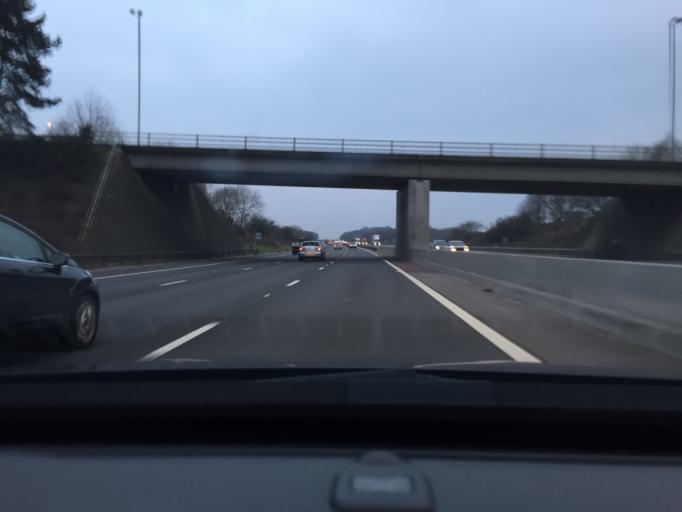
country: GB
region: England
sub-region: Hampshire
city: Botley
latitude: 50.8743
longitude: -1.2525
